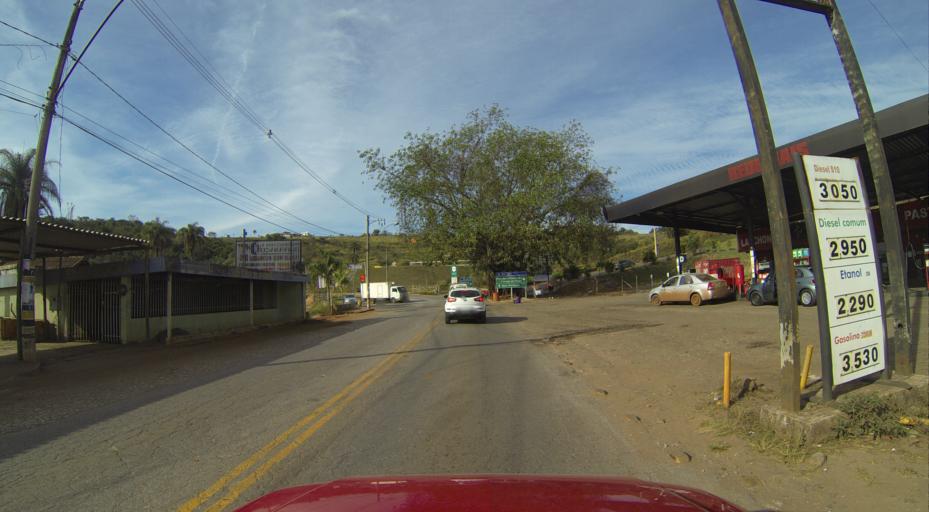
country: BR
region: Minas Gerais
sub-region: Brumadinho
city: Brumadinho
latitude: -20.1363
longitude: -44.1995
